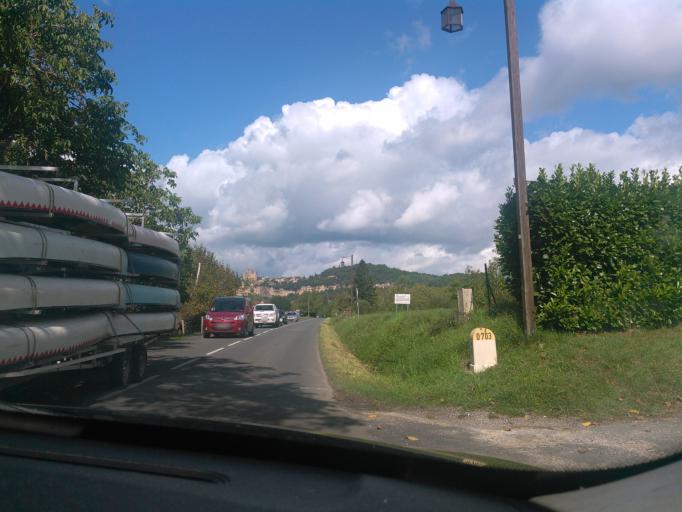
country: FR
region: Aquitaine
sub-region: Departement de la Dordogne
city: Cenac-et-Saint-Julien
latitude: 44.8256
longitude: 1.1548
